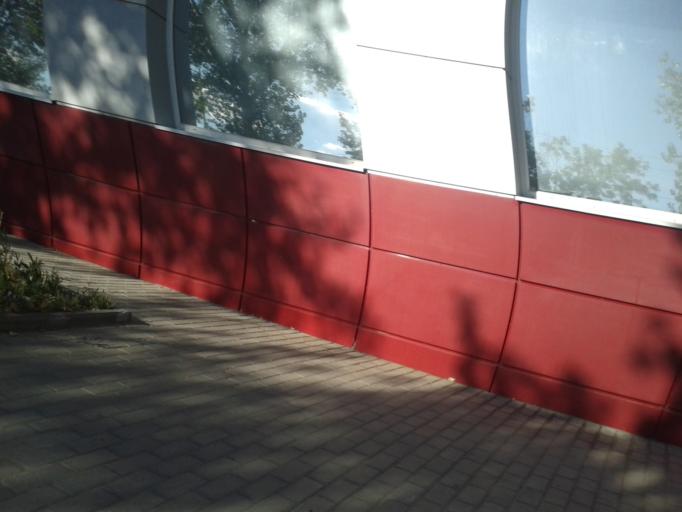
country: RU
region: Volgograd
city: Volgograd
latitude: 48.7467
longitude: 44.4886
